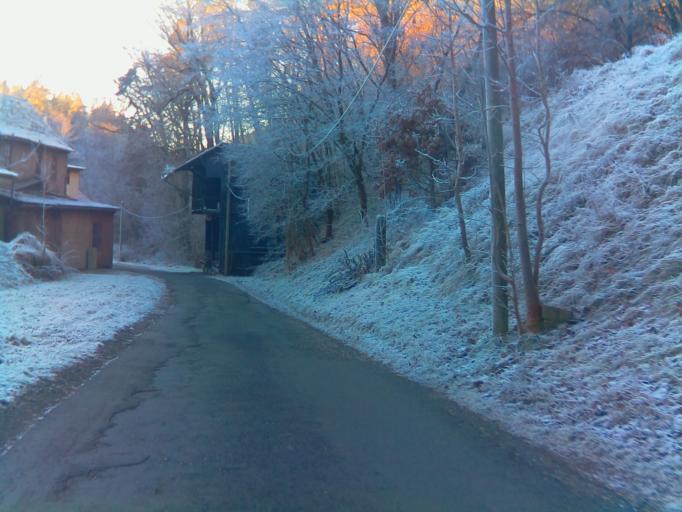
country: DE
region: Thuringia
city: Lindig
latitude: 50.7835
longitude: 11.6077
